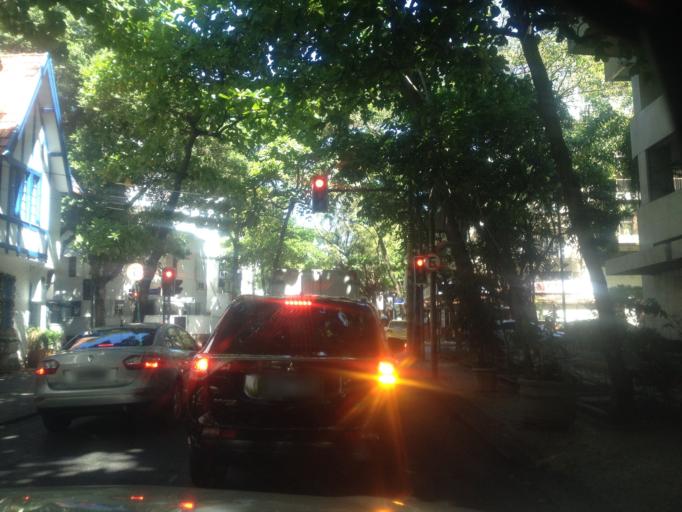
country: BR
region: Rio de Janeiro
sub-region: Rio De Janeiro
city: Rio de Janeiro
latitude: -22.9814
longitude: -43.2089
